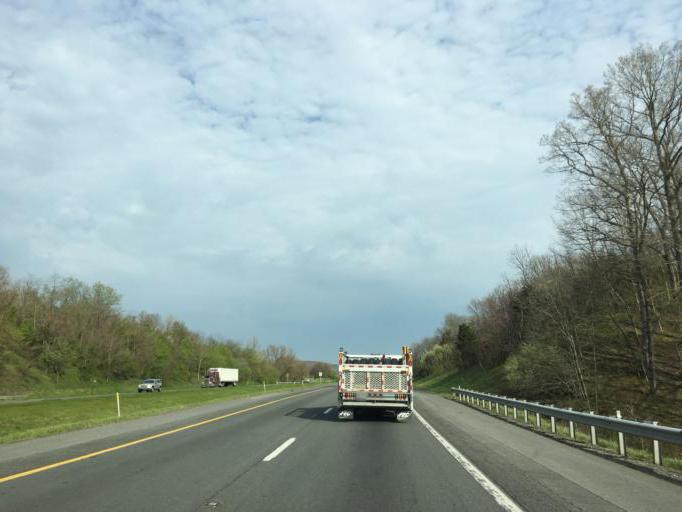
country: US
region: Maryland
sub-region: Frederick County
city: Myersville
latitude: 39.4912
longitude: -77.5612
